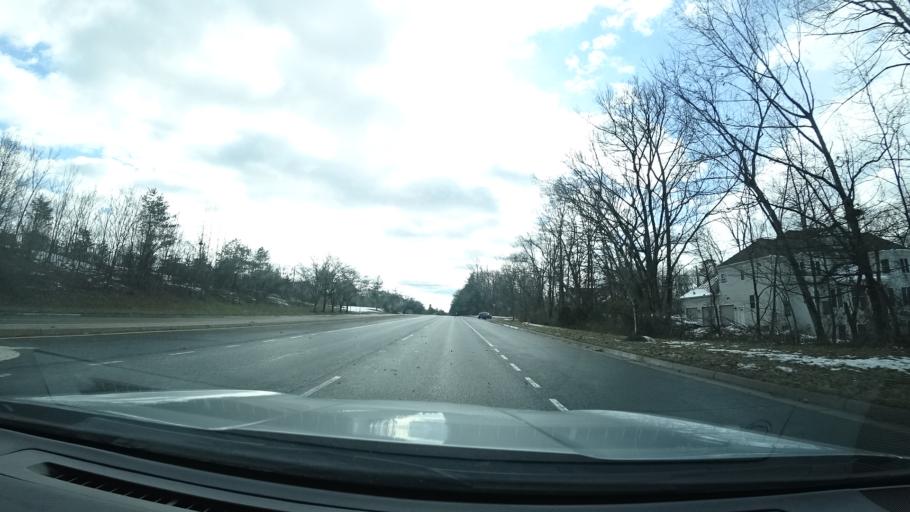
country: US
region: Virginia
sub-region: Loudoun County
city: Sugarland Run
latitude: 39.0216
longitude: -77.3628
